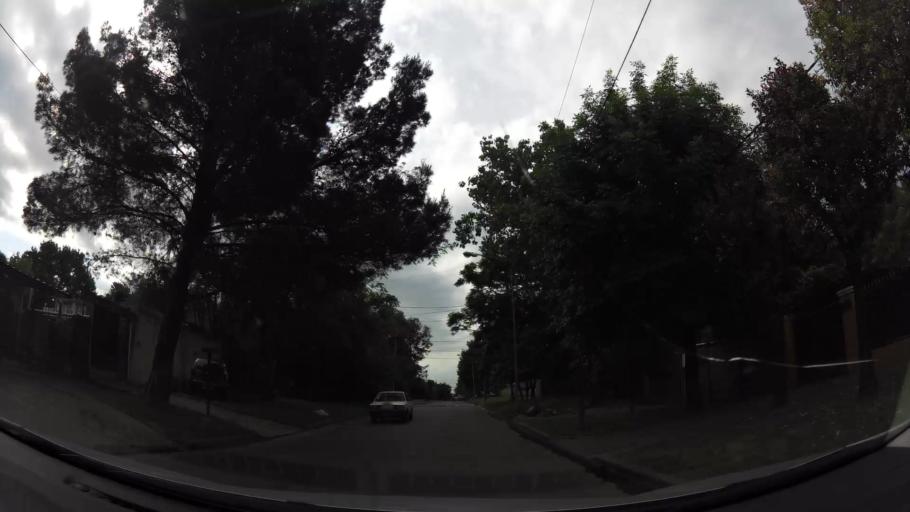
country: AR
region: Buenos Aires
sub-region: Partido de Tigre
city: Tigre
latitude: -34.4776
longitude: -58.6416
